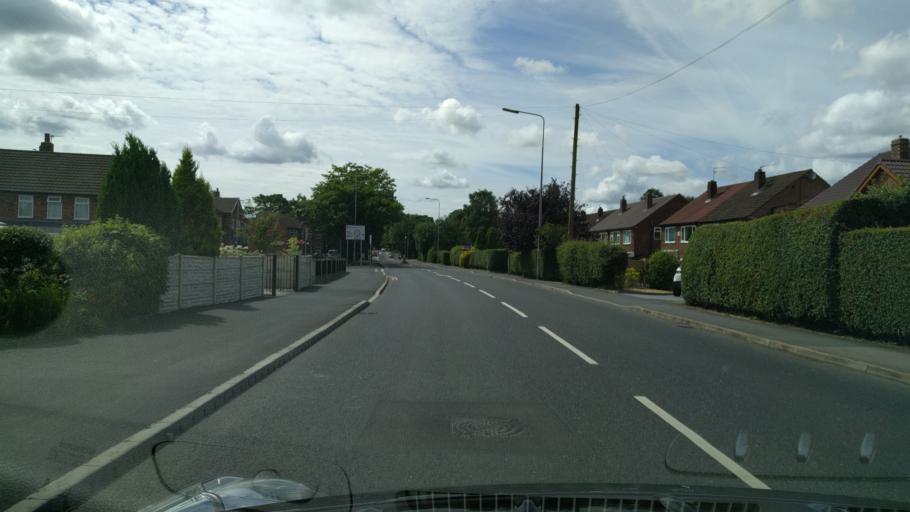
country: GB
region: England
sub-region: Warrington
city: Culcheth
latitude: 53.4531
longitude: -2.5153
